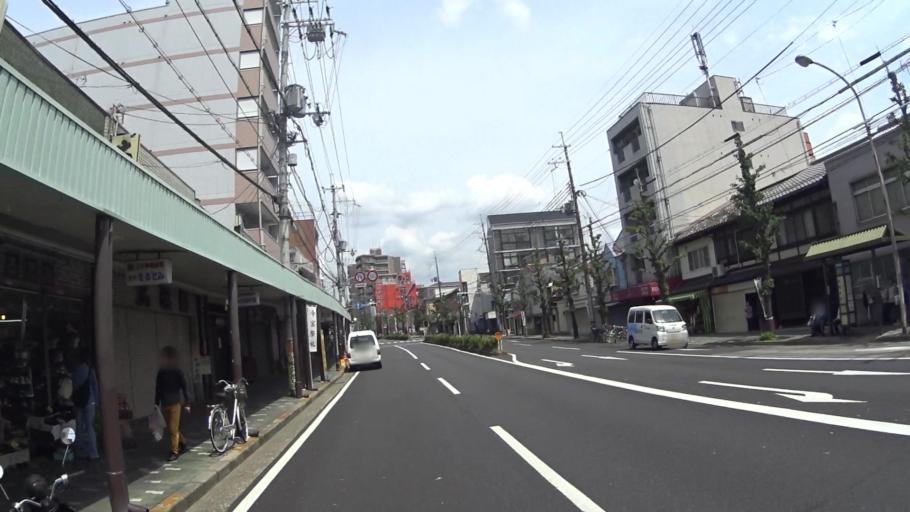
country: JP
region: Kyoto
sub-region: Kyoto-shi
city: Kamigyo-ku
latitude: 35.0344
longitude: 135.7412
